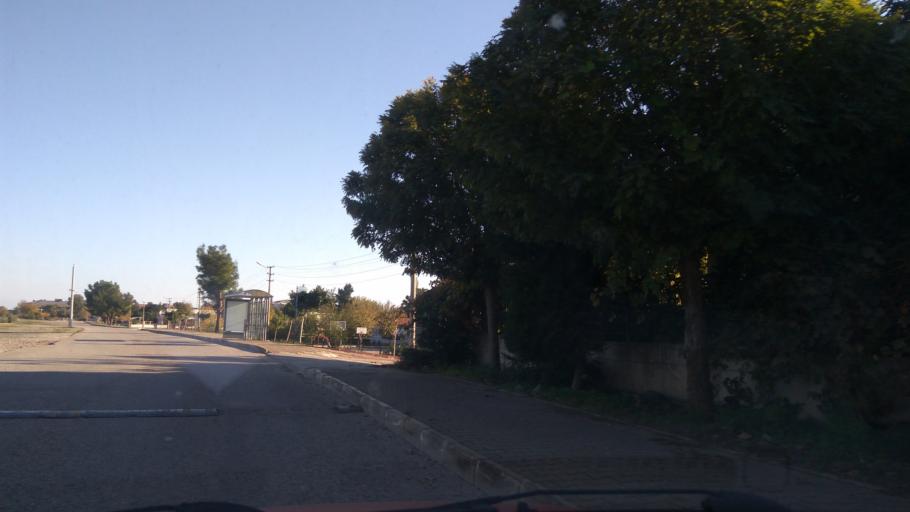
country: TR
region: Antalya
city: Kemer
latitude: 36.5685
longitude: 30.5611
